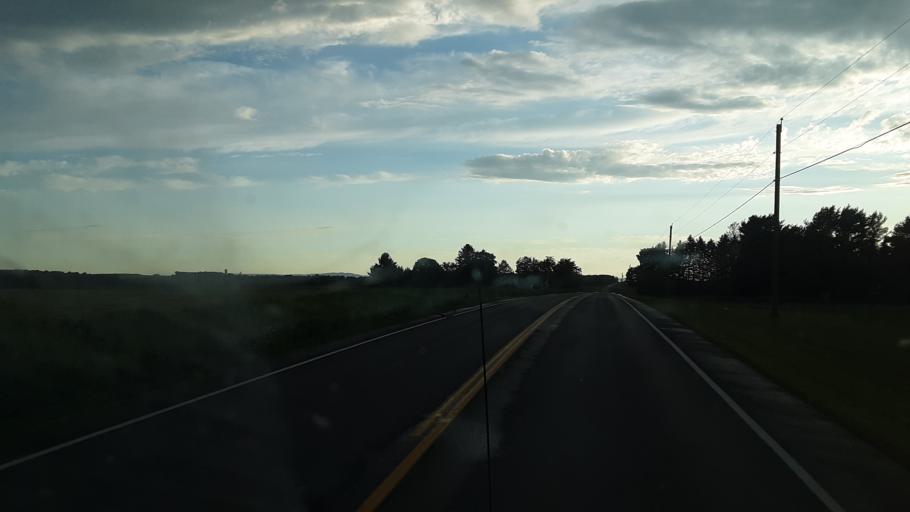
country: US
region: Maine
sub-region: Aroostook County
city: Presque Isle
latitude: 46.6752
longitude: -67.9579
